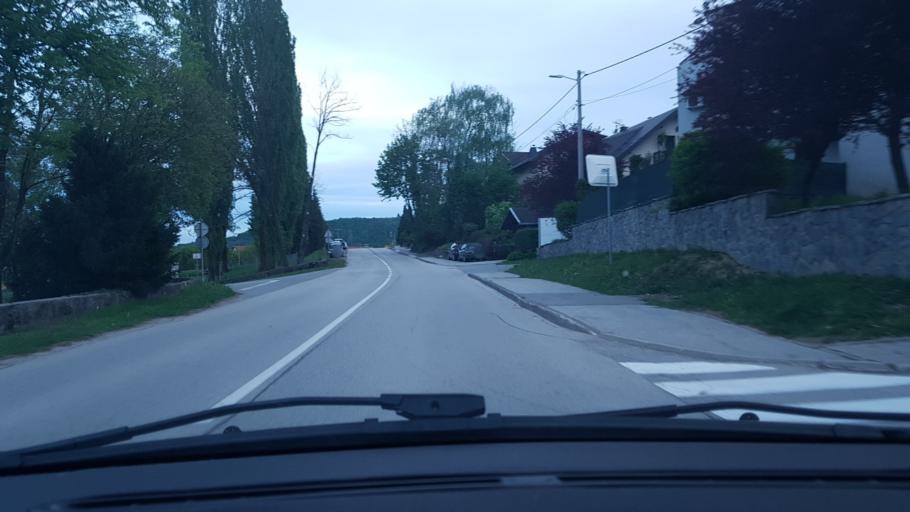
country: HR
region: Zagrebacka
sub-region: Grad Samobor
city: Samobor
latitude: 45.7950
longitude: 15.7194
